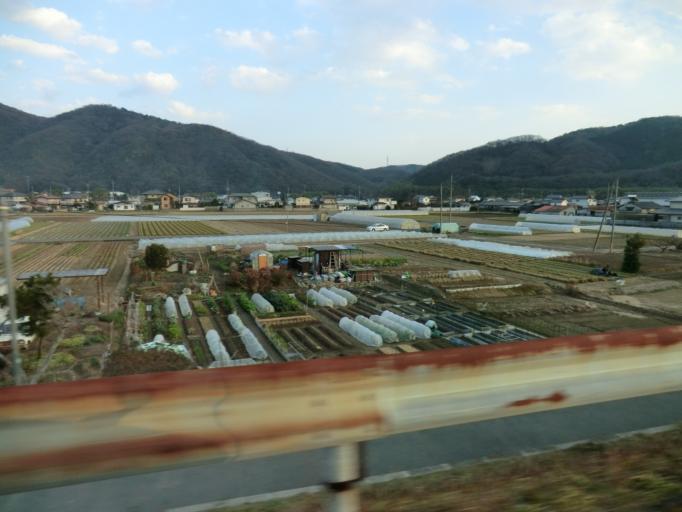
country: JP
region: Okayama
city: Okayama-shi
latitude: 34.7194
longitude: 133.9748
